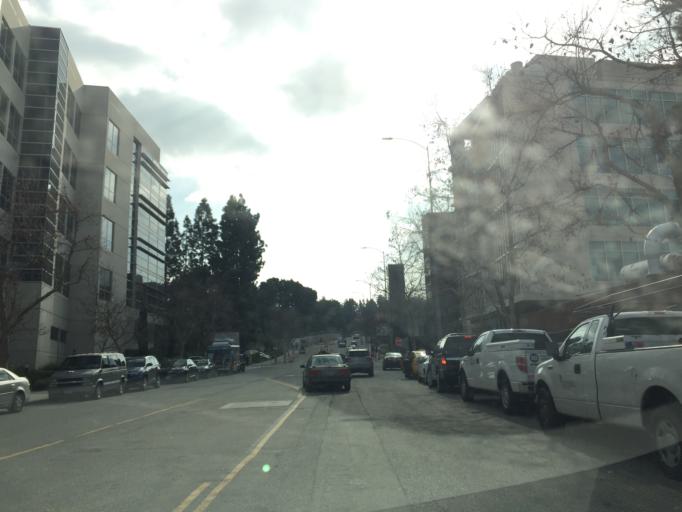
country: US
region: California
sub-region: Los Angeles County
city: Boyle Heights
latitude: 34.0630
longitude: -118.2029
